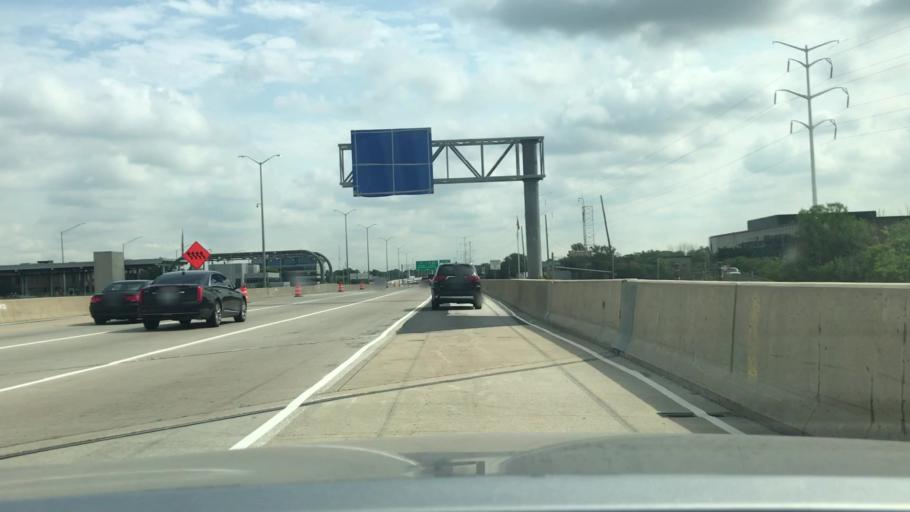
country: US
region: Illinois
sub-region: DuPage County
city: Oak Brook
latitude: 41.8472
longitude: -87.9420
